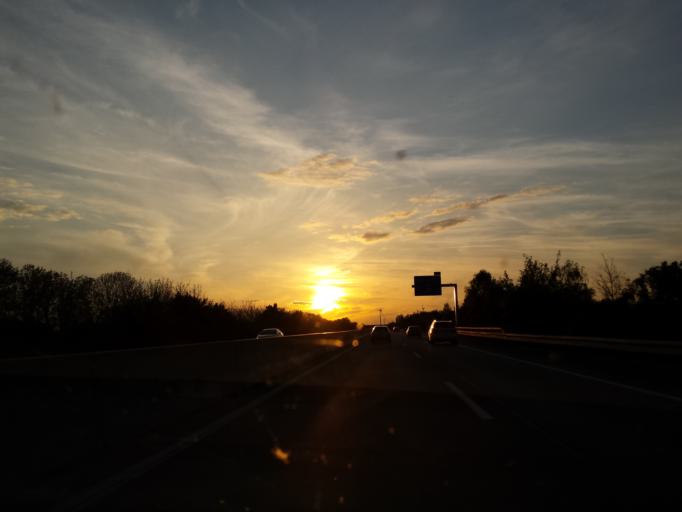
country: AT
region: Burgenland
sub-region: Politischer Bezirk Neusiedl am See
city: Bruckneudorf
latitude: 48.0341
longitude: 16.8204
